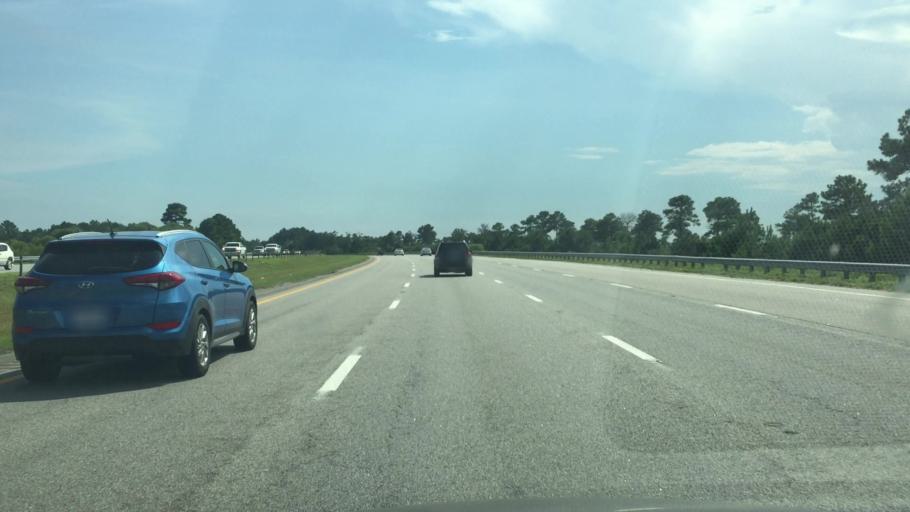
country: US
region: South Carolina
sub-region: Horry County
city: North Myrtle Beach
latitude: 33.7934
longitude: -78.8029
